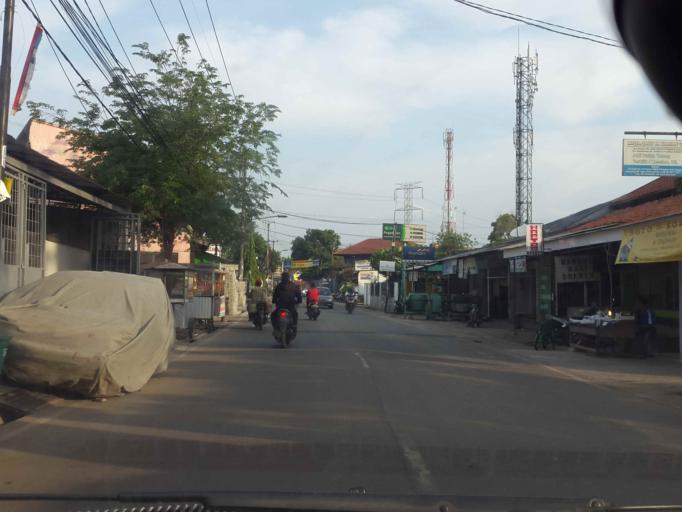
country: ID
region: West Java
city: Ciputat
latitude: -6.2579
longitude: 106.7064
